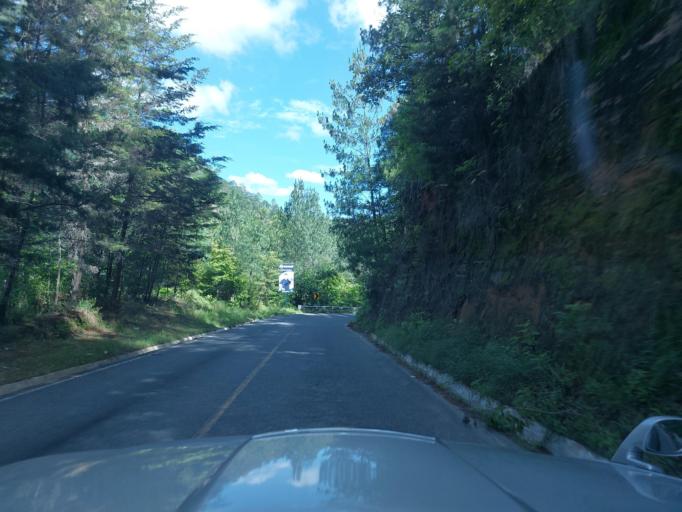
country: GT
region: Chimaltenango
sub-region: Municipio de Santa Cruz Balanya
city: Santa Cruz Balanya
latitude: 14.6923
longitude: -90.8977
